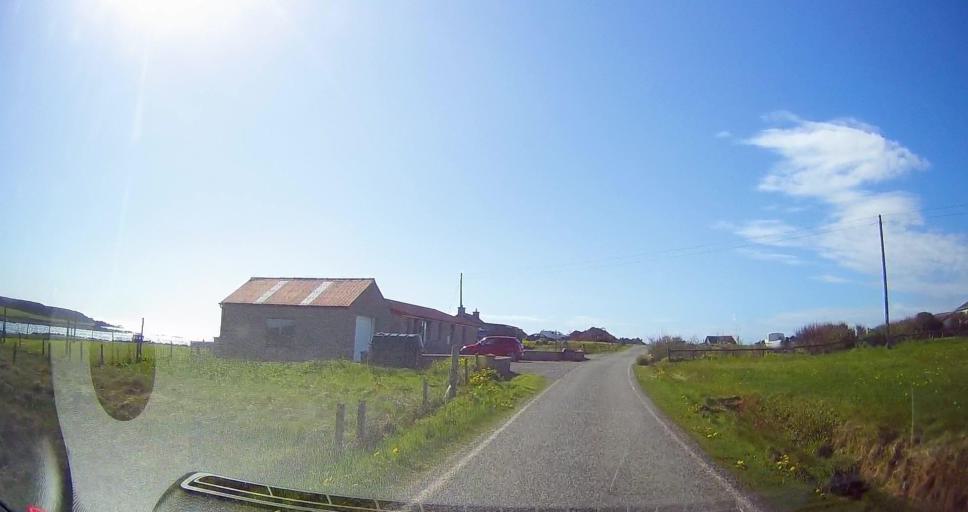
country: GB
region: Scotland
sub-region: Shetland Islands
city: Sandwick
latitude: 60.0390
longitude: -1.2181
